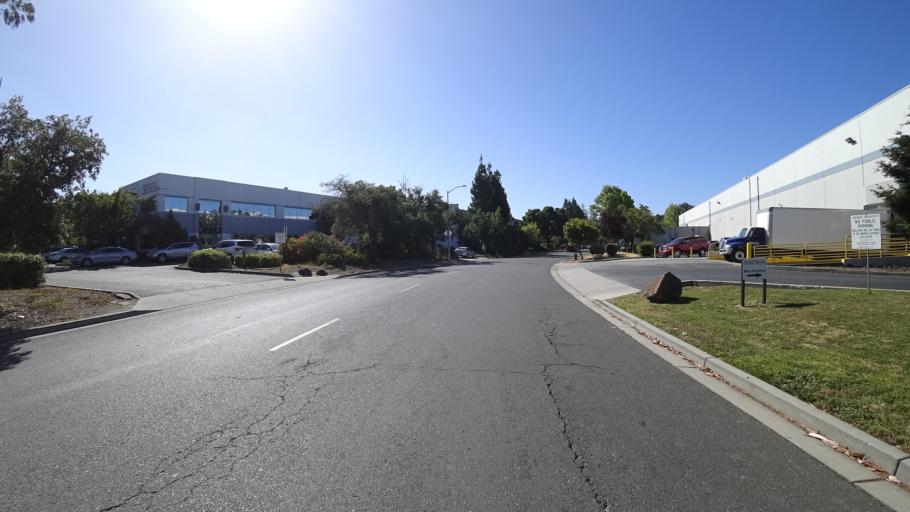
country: US
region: California
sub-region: Alameda County
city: Union City
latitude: 37.6191
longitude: -122.0505
